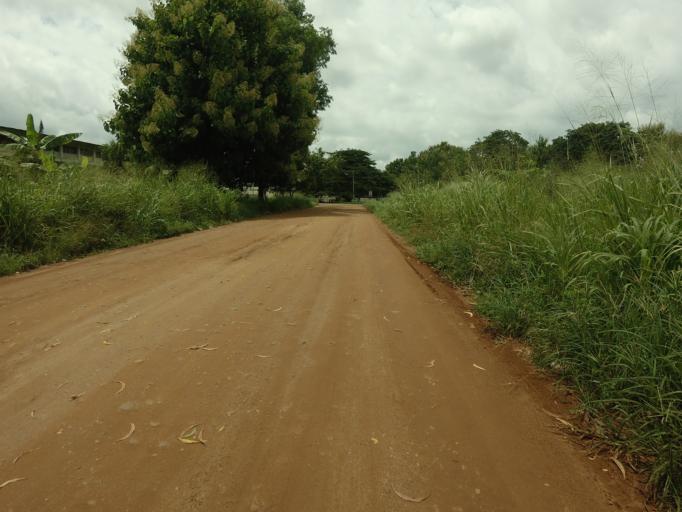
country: GH
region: Volta
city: Ho
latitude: 6.5893
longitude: 0.4691
